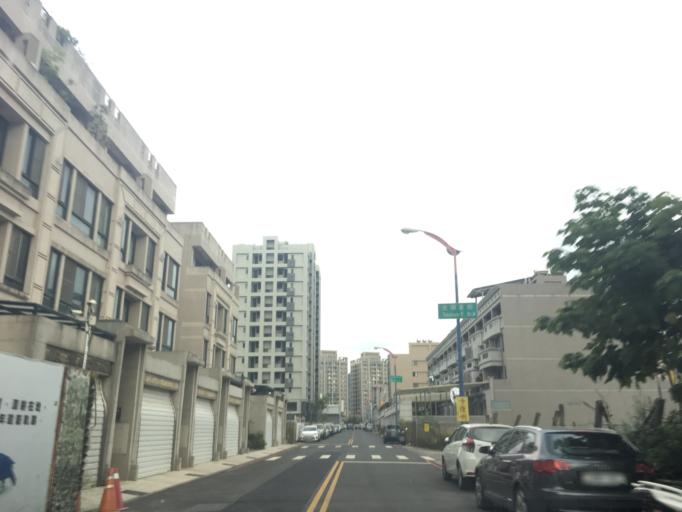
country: TW
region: Taiwan
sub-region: Taichung City
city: Taichung
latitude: 24.1613
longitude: 120.7229
